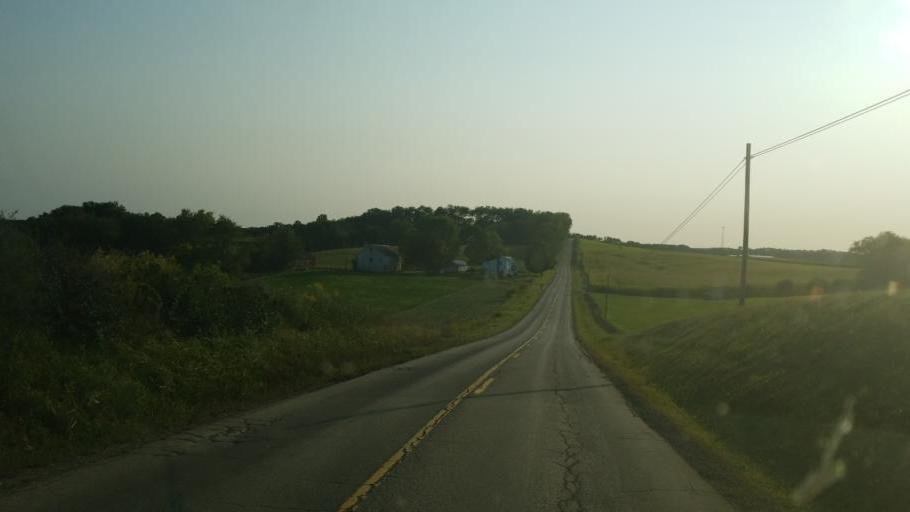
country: US
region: Ohio
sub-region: Wayne County
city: Apple Creek
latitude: 40.6851
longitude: -81.8570
